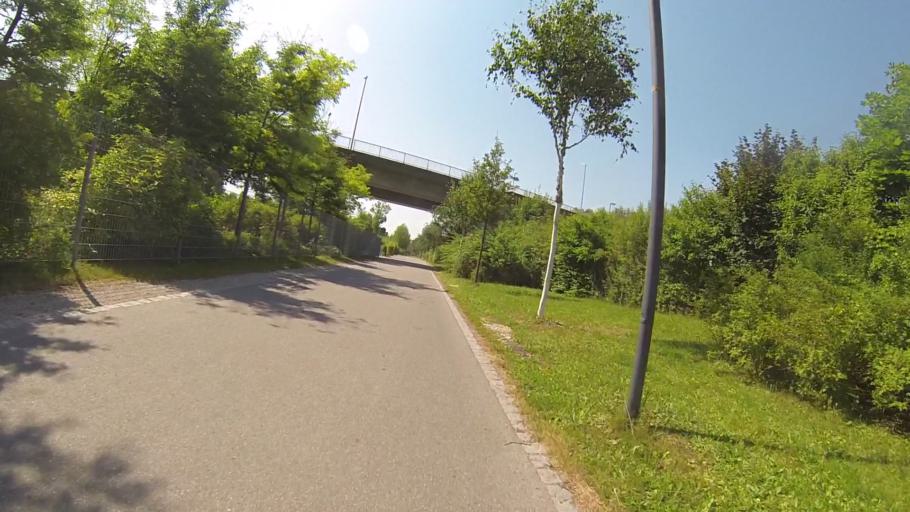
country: DE
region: Baden-Wuerttemberg
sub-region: Regierungsbezirk Stuttgart
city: Heidenheim an der Brenz
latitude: 48.6886
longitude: 10.1557
